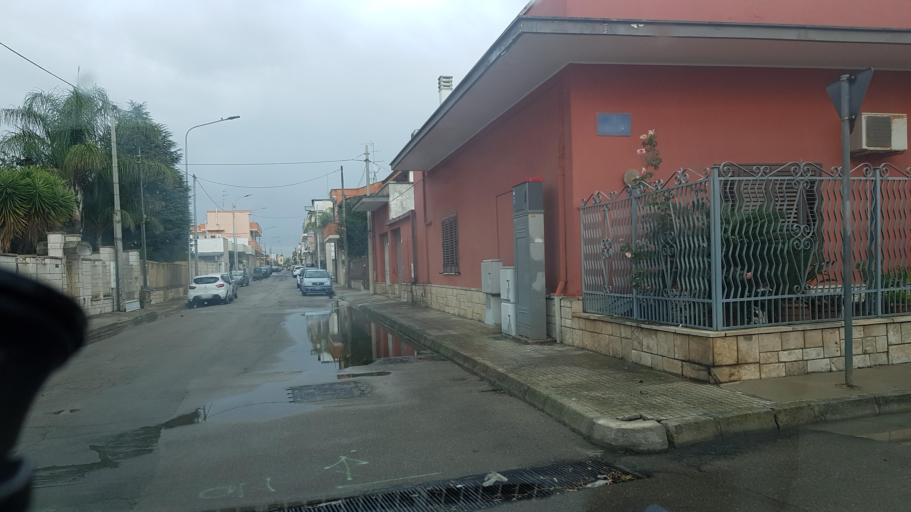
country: IT
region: Apulia
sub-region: Provincia di Lecce
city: Carmiano
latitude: 40.3382
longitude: 18.0447
